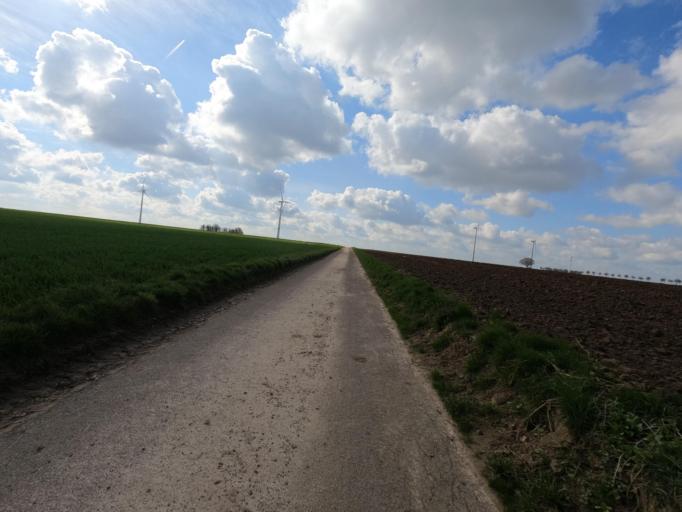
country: DE
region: North Rhine-Westphalia
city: Erkelenz
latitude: 51.0233
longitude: 6.3449
